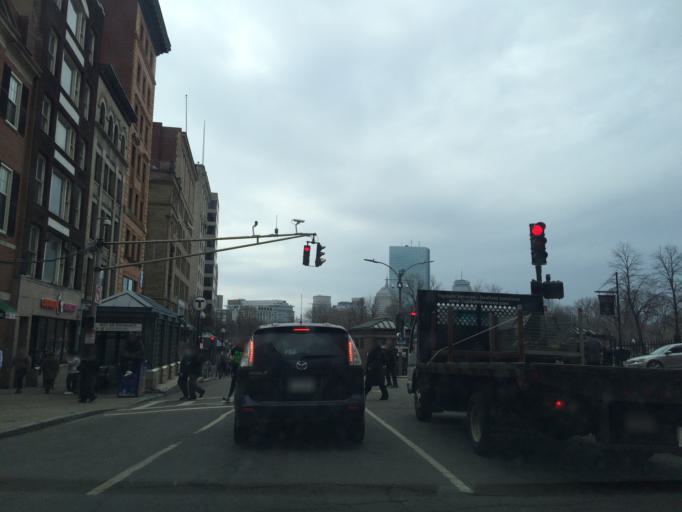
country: US
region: Massachusetts
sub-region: Suffolk County
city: Boston
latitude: 42.3568
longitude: -71.0618
